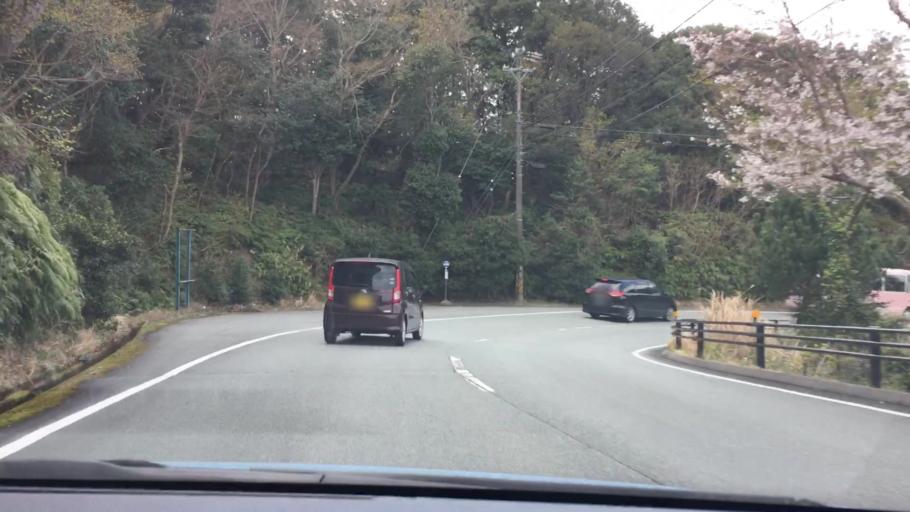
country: JP
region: Mie
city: Toba
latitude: 34.4493
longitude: 136.8791
